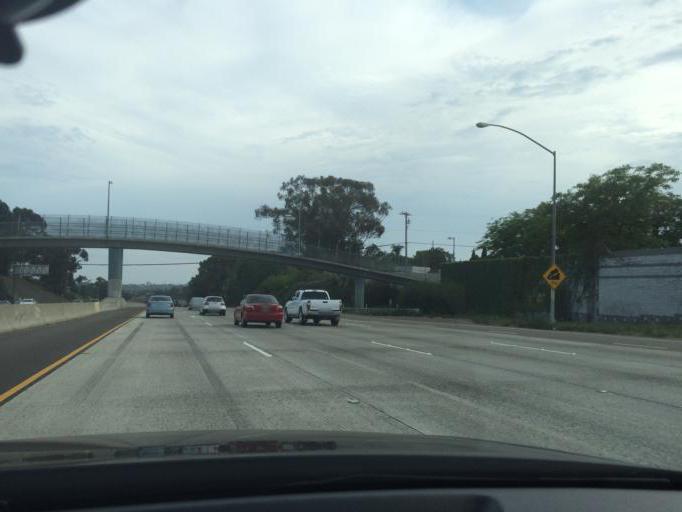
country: US
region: California
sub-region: San Diego County
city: San Diego
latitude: 32.7882
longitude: -117.1603
